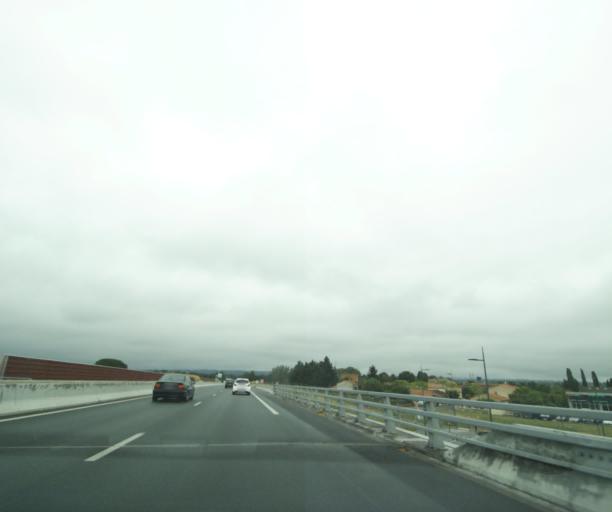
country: FR
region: Midi-Pyrenees
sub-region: Departement du Tarn
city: Puygouzon
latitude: 43.9210
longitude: 2.1681
